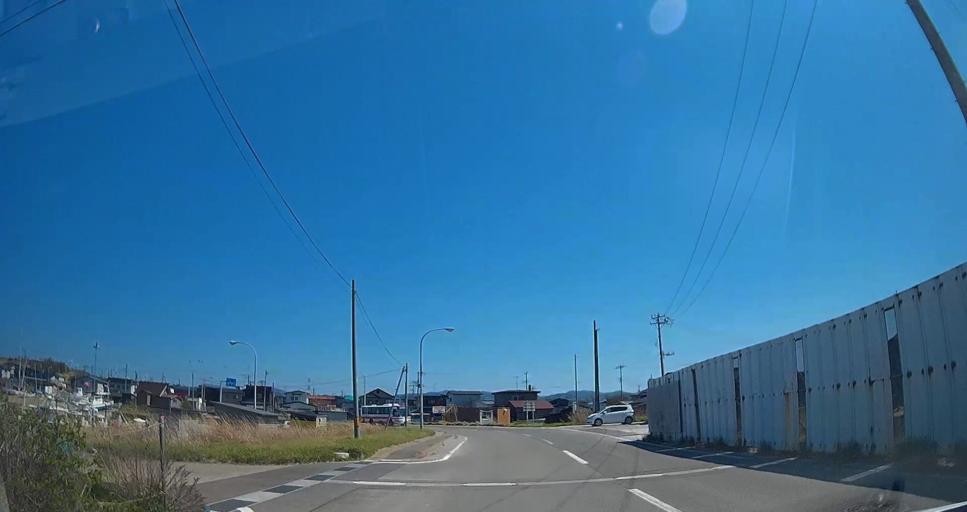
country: JP
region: Hokkaido
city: Hakodate
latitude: 41.5232
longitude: 140.8974
